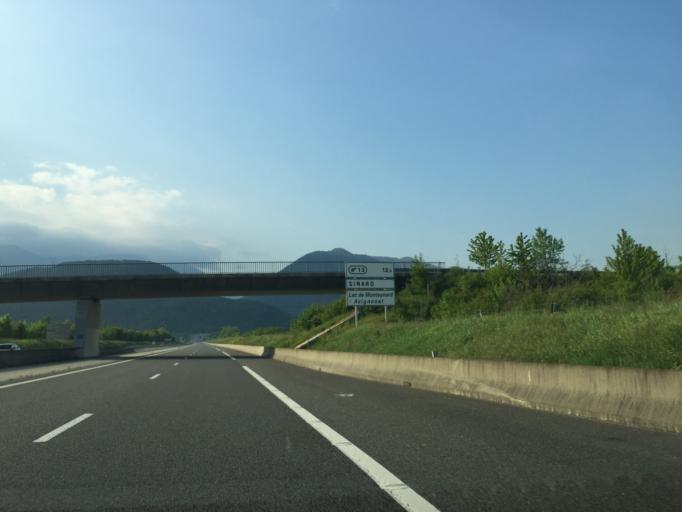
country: FR
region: Rhone-Alpes
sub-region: Departement de l'Isere
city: Vif
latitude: 45.0680
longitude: 5.6808
